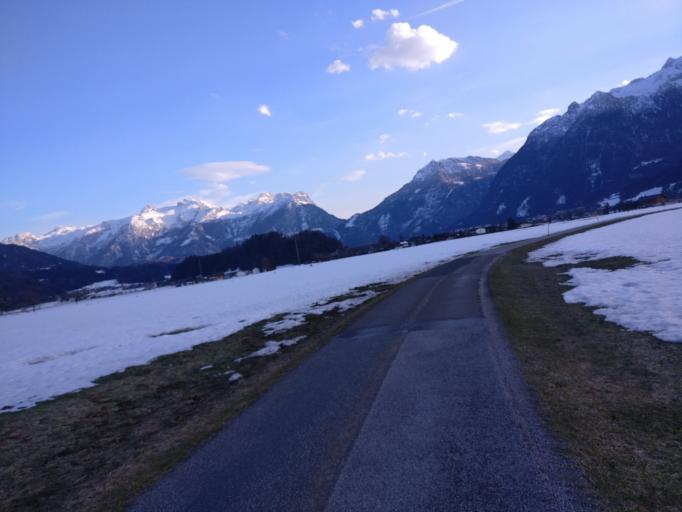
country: AT
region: Salzburg
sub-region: Politischer Bezirk Hallein
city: Kuchl
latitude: 47.6464
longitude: 13.1550
